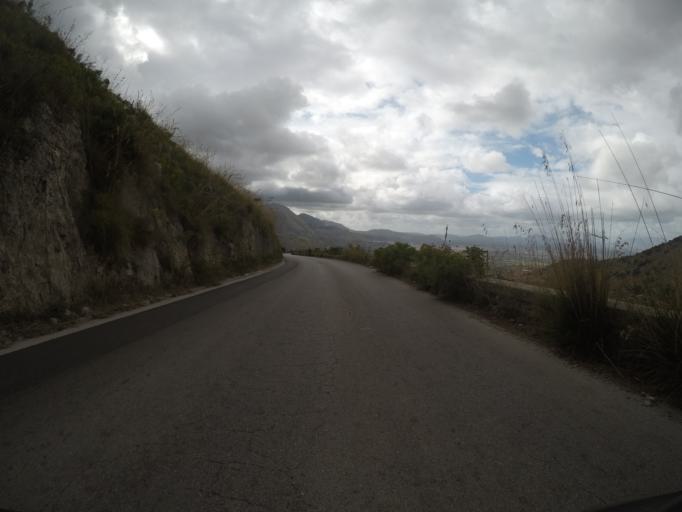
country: IT
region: Sicily
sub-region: Palermo
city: Montelepre
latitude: 38.0974
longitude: 13.1672
